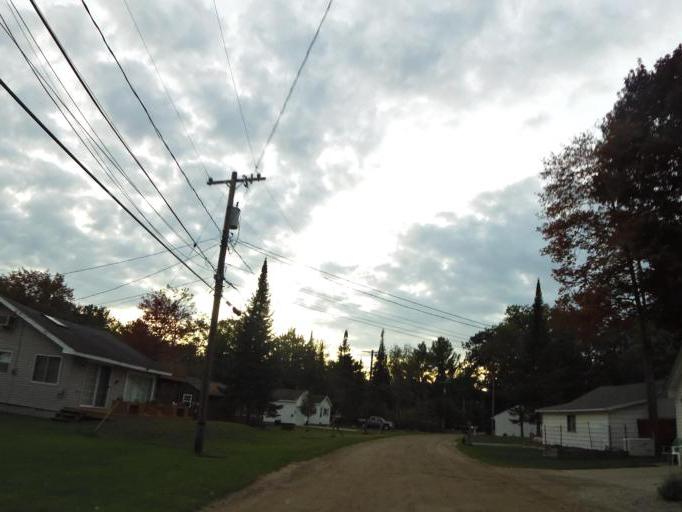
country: US
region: Michigan
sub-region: Roscommon County
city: Saint Helen
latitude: 44.3547
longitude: -84.4851
